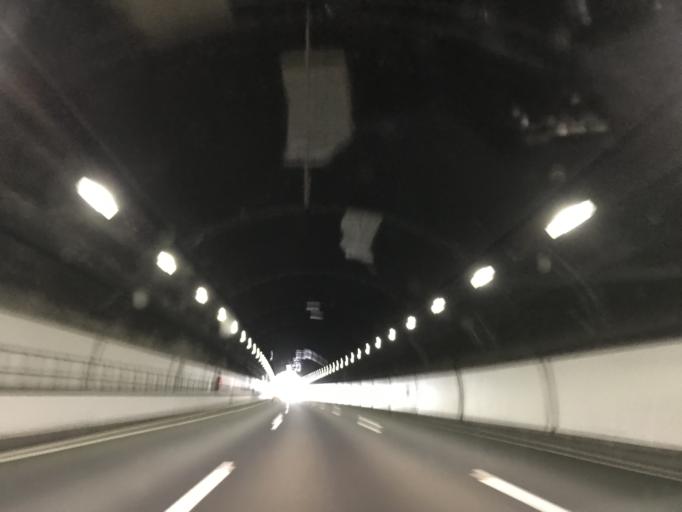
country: JP
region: Shizuoka
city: Gotemba
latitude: 35.3592
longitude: 139.0359
